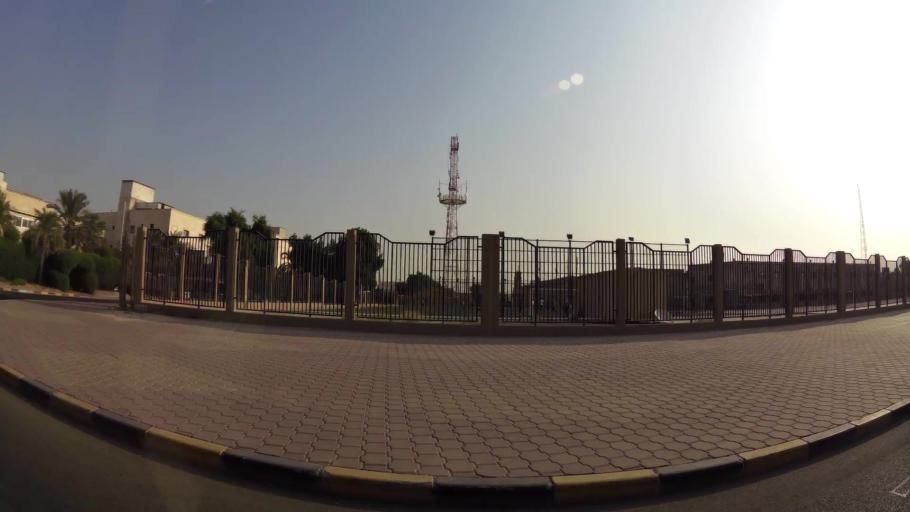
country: KW
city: Bayan
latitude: 29.2994
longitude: 48.0500
